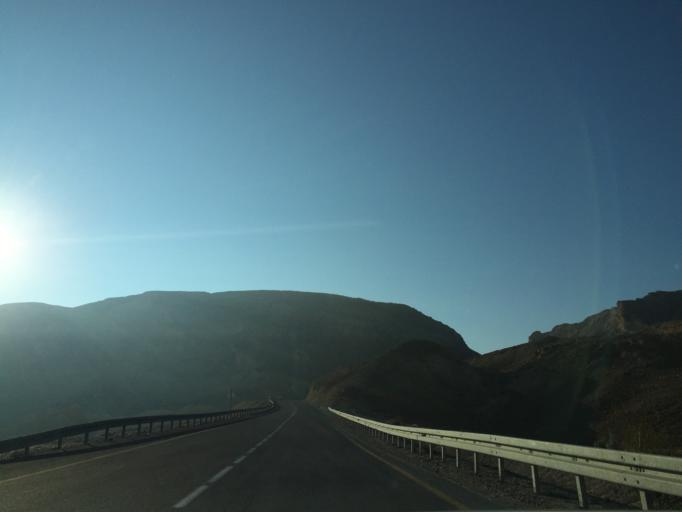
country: IL
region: Southern District
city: Mitzpe Ramon
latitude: 30.3242
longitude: 34.9559
